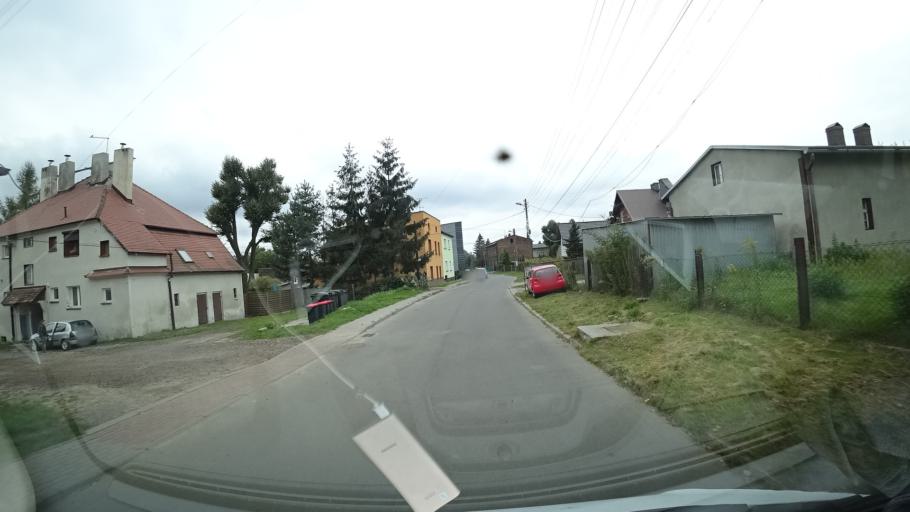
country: PL
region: Silesian Voivodeship
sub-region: Ruda Slaska
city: Ruda Slaska
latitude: 50.2668
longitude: 18.8225
